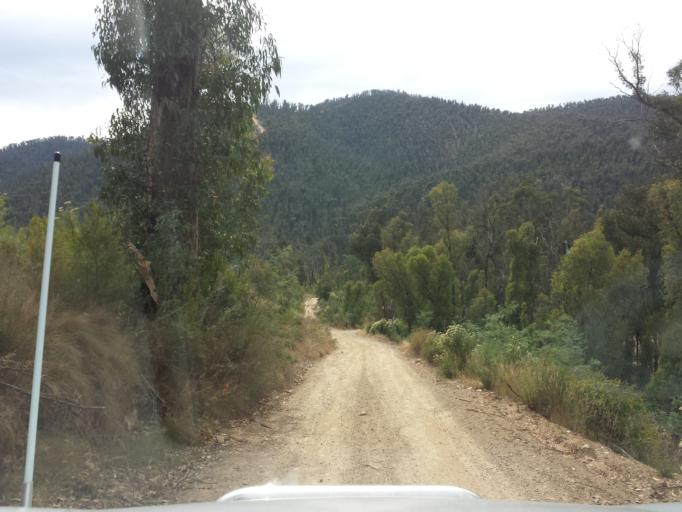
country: AU
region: Victoria
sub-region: Latrobe
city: Moe
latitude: -37.7604
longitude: 146.3991
